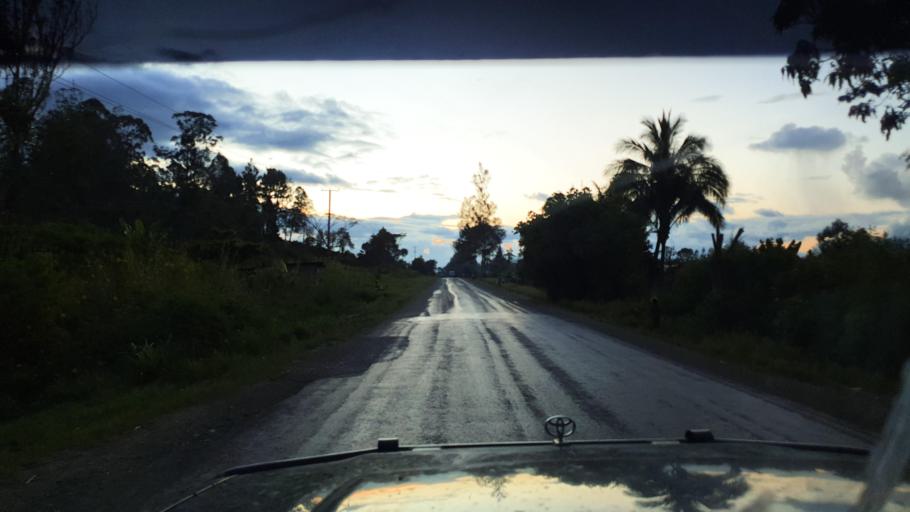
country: PG
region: Jiwaka
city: Minj
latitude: -5.8390
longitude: 144.5757
